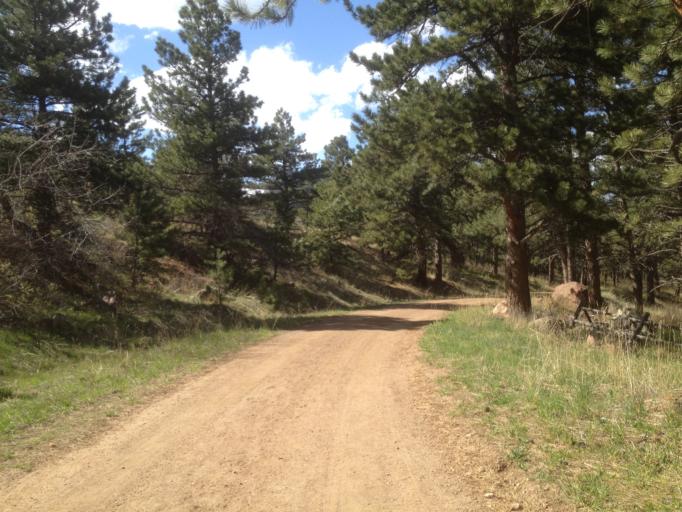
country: US
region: Colorado
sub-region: Boulder County
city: Boulder
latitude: 39.9205
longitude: -105.2708
